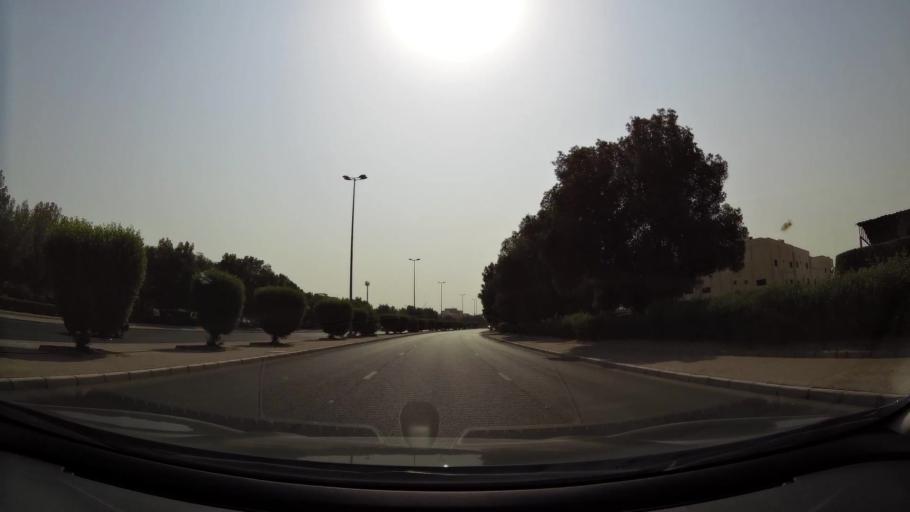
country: KW
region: Al Asimah
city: Ar Rabiyah
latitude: 29.2831
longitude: 47.8859
